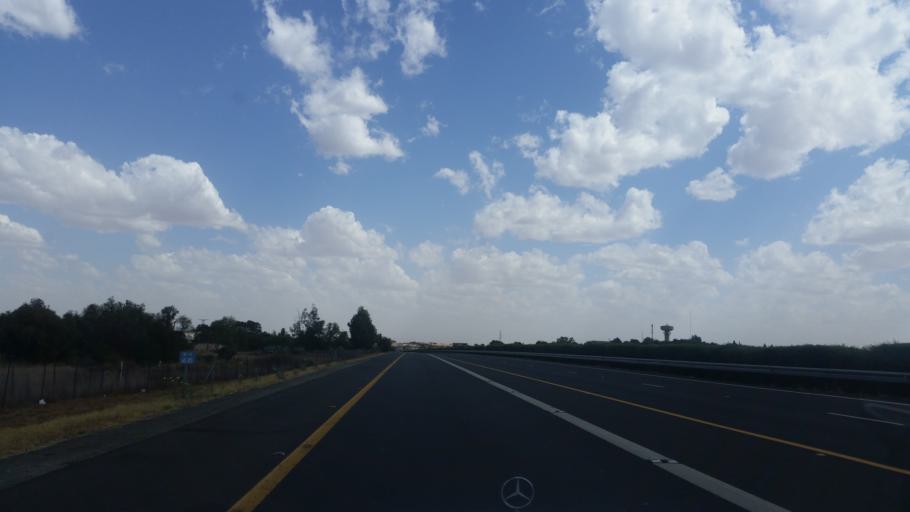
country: ZA
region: Orange Free State
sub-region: Mangaung Metropolitan Municipality
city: Bloemfontein
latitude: -29.0772
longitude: 26.1807
